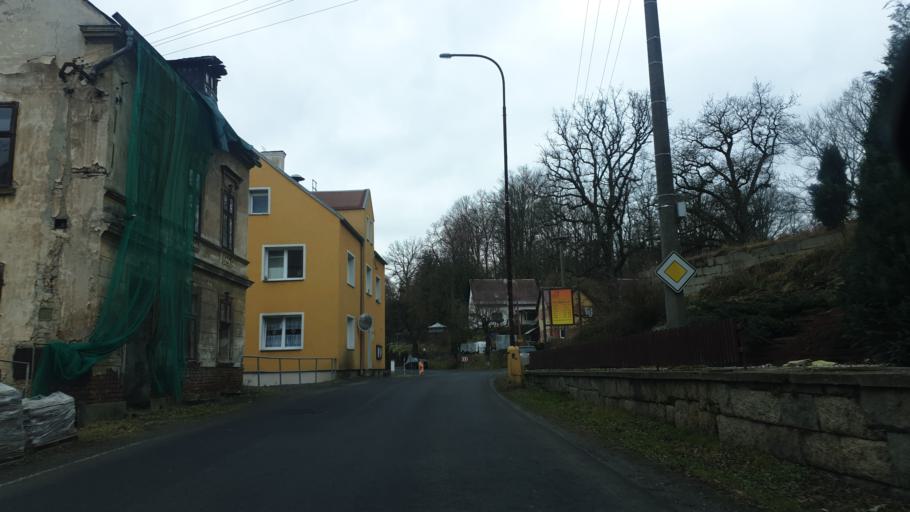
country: CZ
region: Karlovarsky
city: As
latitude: 50.2552
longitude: 12.2042
